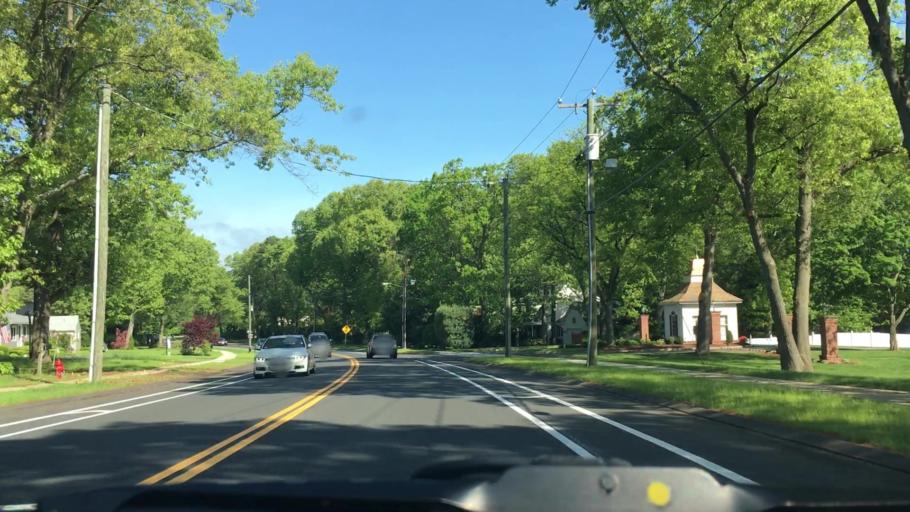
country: US
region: Massachusetts
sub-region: Hampden County
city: Longmeadow
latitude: 42.0651
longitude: -72.5529
